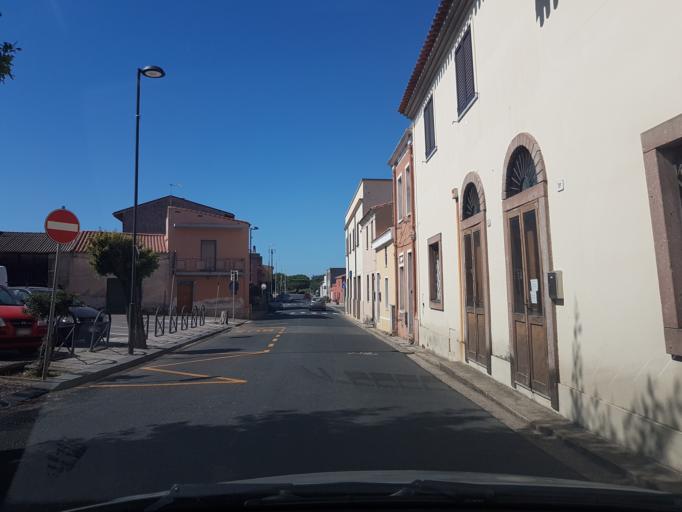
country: IT
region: Sardinia
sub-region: Provincia di Oristano
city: Riola Sardo
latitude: 39.9959
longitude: 8.5391
